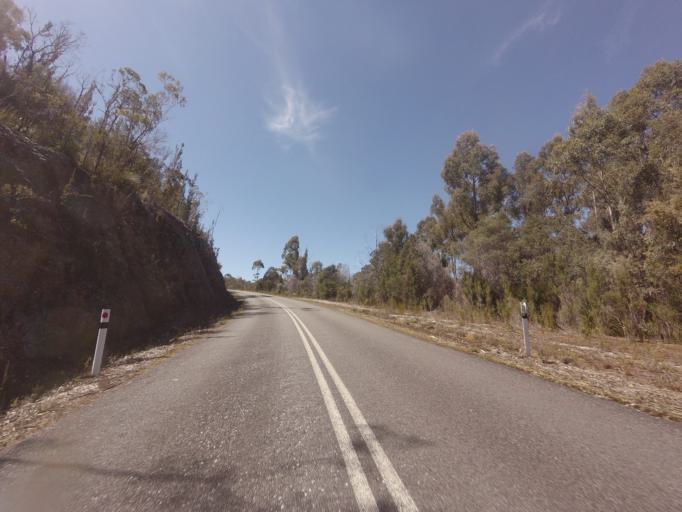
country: AU
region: Tasmania
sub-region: Huon Valley
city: Geeveston
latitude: -42.8571
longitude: 146.2323
